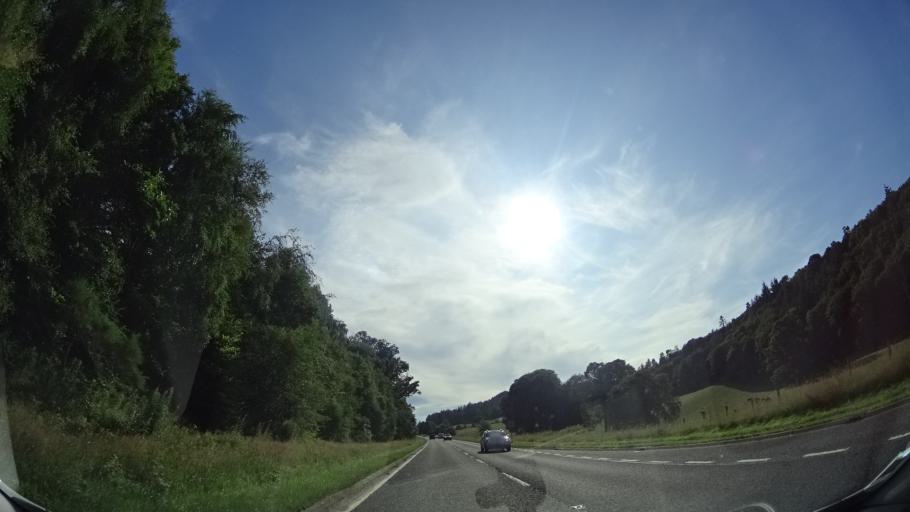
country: GB
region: Scotland
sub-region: Highland
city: Conon Bridge
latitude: 57.5711
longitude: -4.4595
